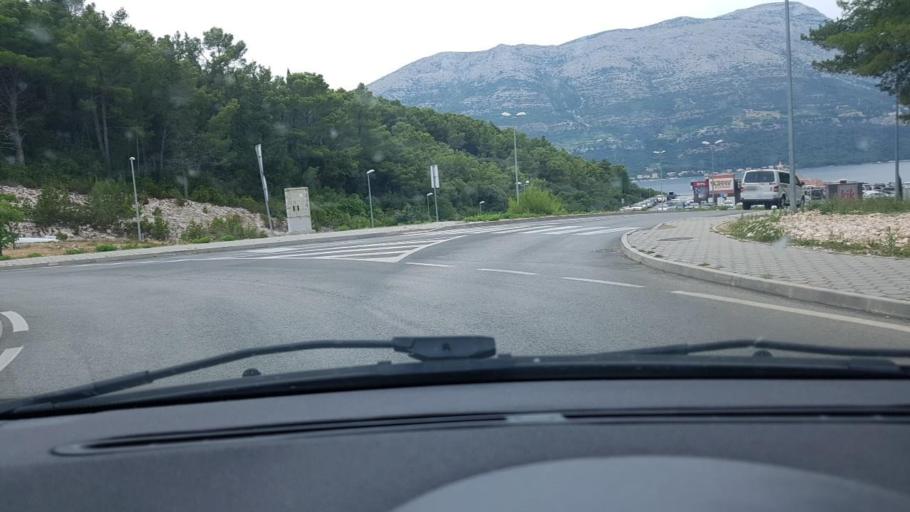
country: HR
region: Dubrovacko-Neretvanska
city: Korcula
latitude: 42.9557
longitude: 17.1316
